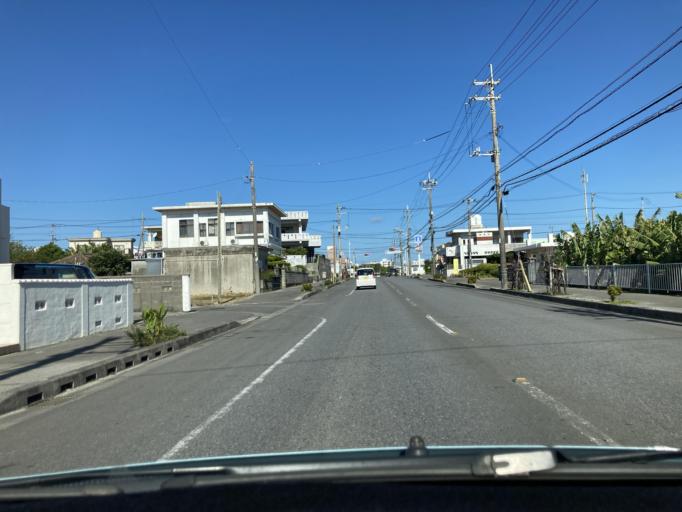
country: JP
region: Okinawa
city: Gushikawa
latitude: 26.3753
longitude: 127.8643
